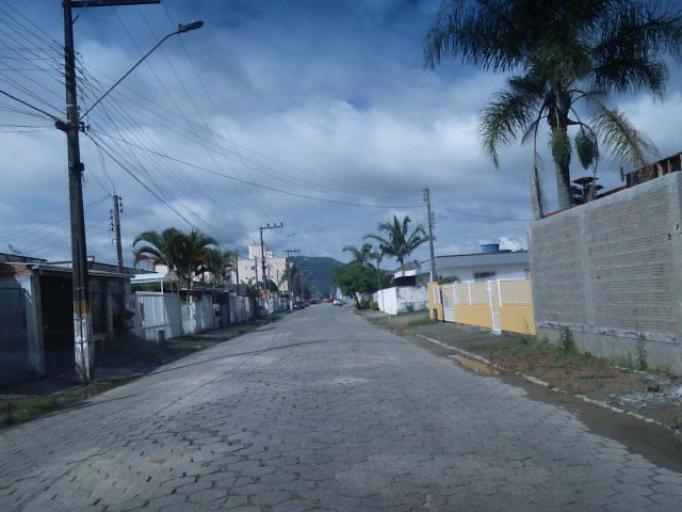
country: BR
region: Santa Catarina
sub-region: Itapema
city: Itapema
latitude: -27.1242
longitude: -48.6166
